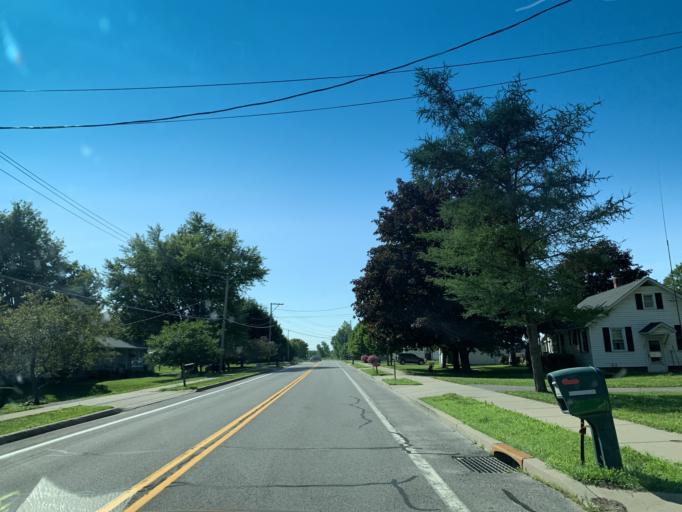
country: US
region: New York
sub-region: Oneida County
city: Sherrill
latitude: 43.1322
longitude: -75.5814
